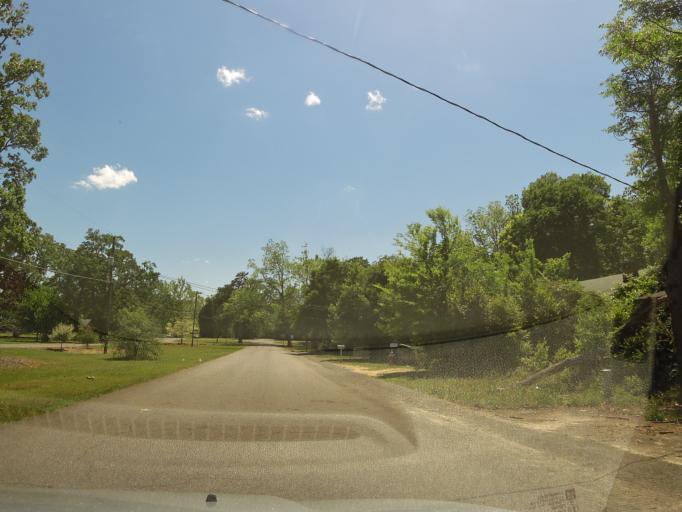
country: US
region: South Carolina
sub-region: Aiken County
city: Aiken
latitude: 33.5619
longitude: -81.7124
